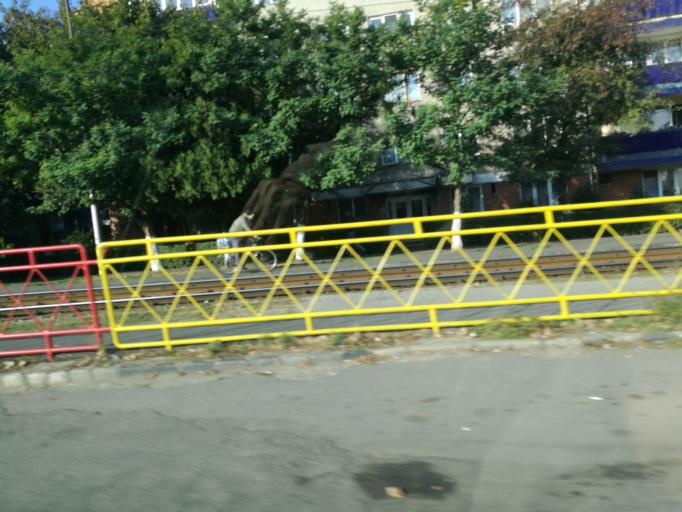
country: RO
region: Bihor
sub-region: Comuna Biharea
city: Oradea
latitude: 47.0402
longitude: 21.9420
